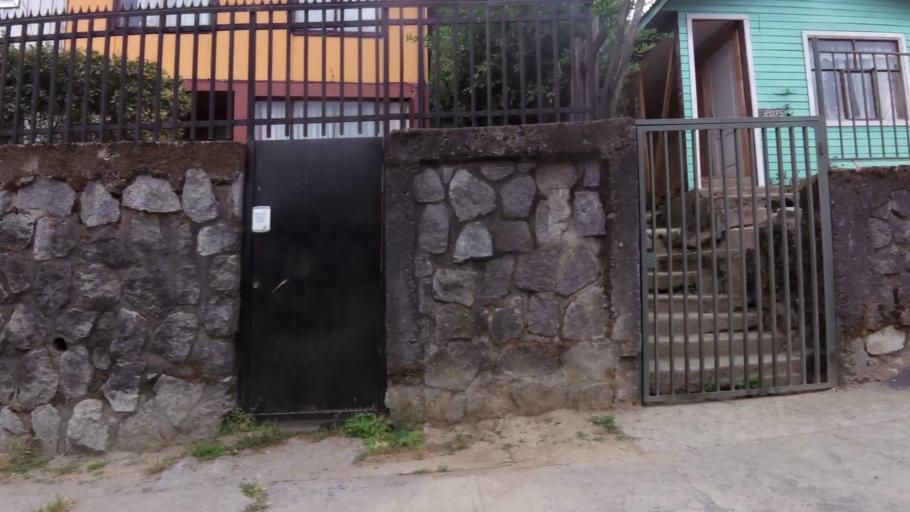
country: CL
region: Biobio
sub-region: Provincia de Concepcion
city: Concepcion
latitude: -36.8116
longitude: -73.0382
